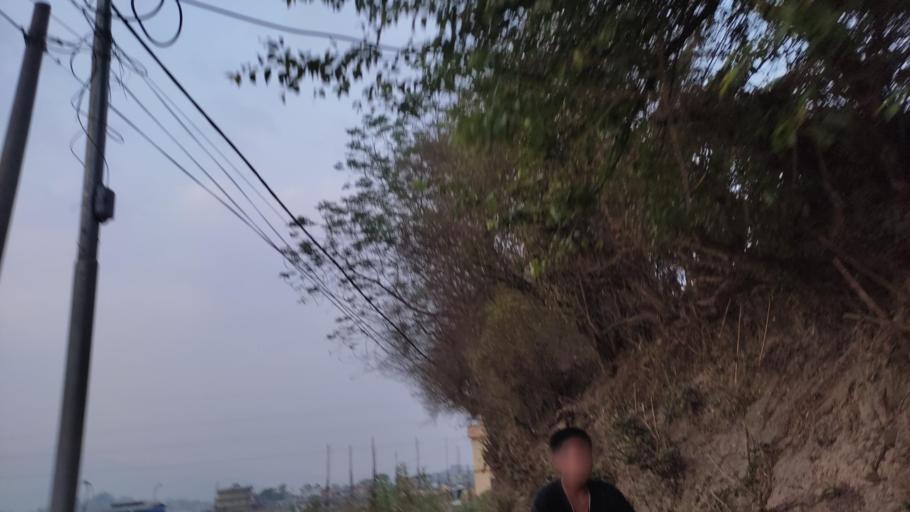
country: NP
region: Central Region
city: Kirtipur
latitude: 27.6701
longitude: 85.2634
